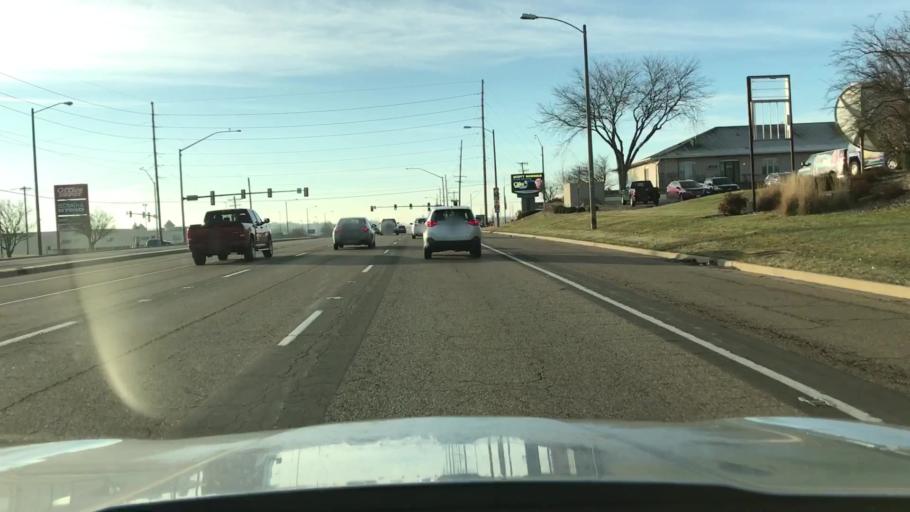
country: US
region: Illinois
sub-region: McLean County
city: Normal
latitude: 40.5118
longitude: -88.9535
